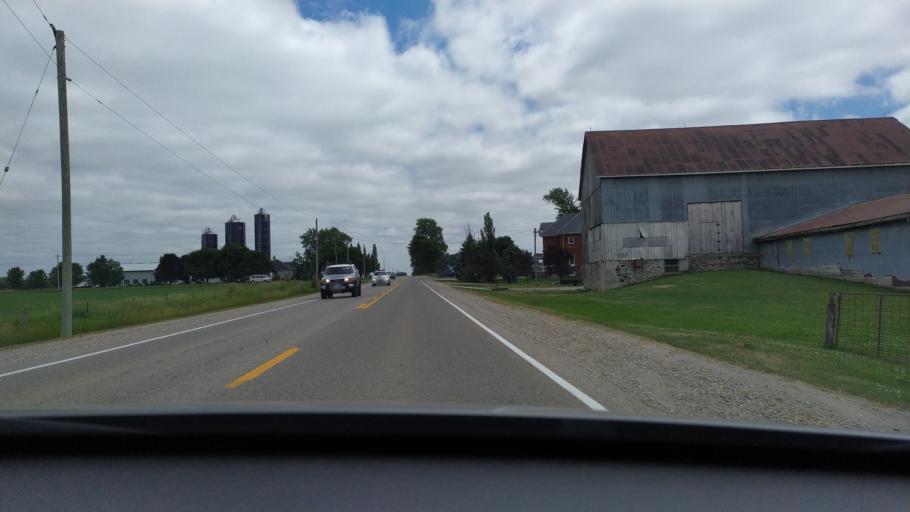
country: CA
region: Ontario
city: Stratford
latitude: 43.3357
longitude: -80.9626
